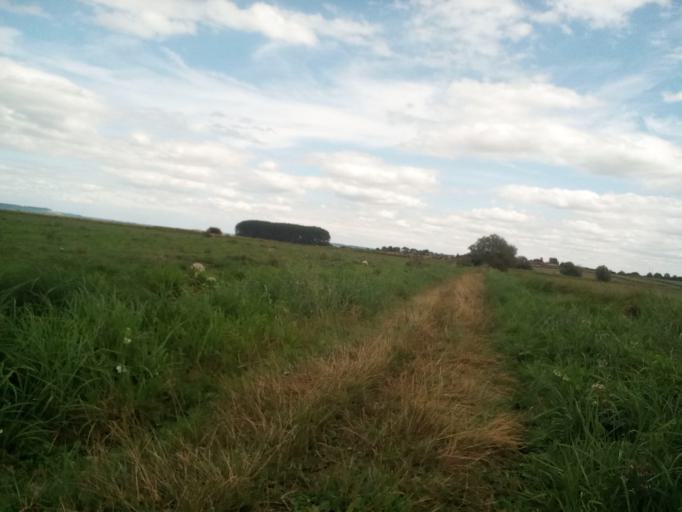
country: FR
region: Lower Normandy
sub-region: Departement du Calvados
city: Troarn
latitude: 49.1743
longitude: -0.1579
